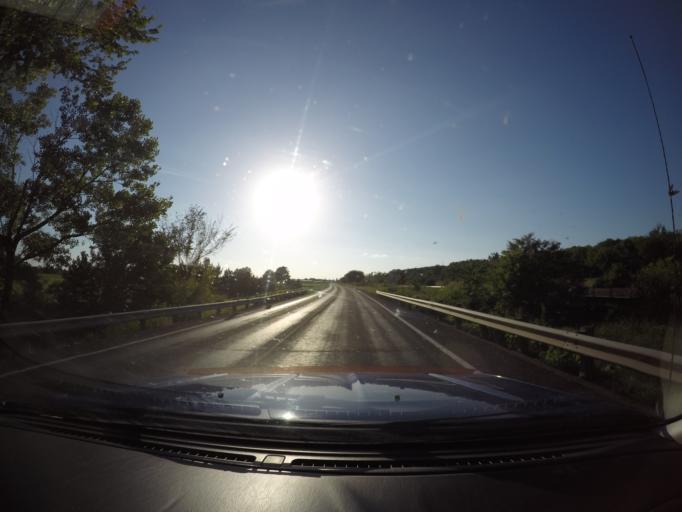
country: US
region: Kansas
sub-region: Pottawatomie County
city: Saint Marys
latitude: 39.1850
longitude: -96.0453
